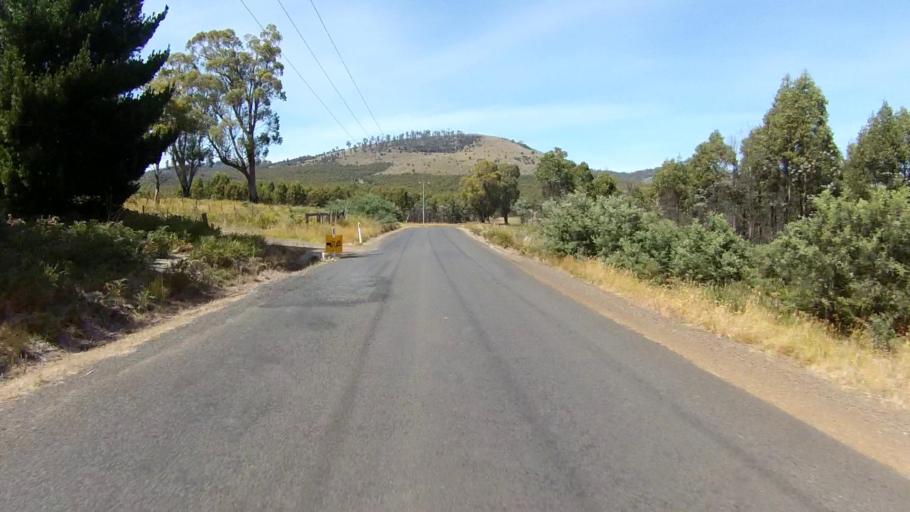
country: AU
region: Tasmania
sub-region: Sorell
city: Sorell
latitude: -42.6177
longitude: 147.7302
